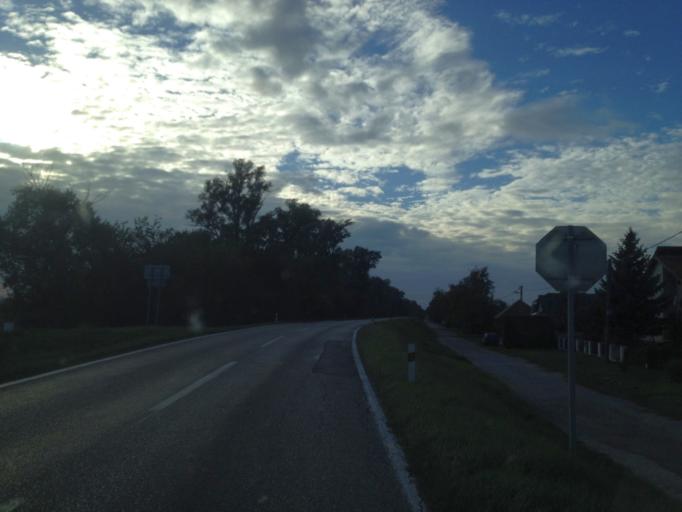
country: HU
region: Komarom-Esztergom
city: Almasfuzito
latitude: 47.7388
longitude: 18.2885
